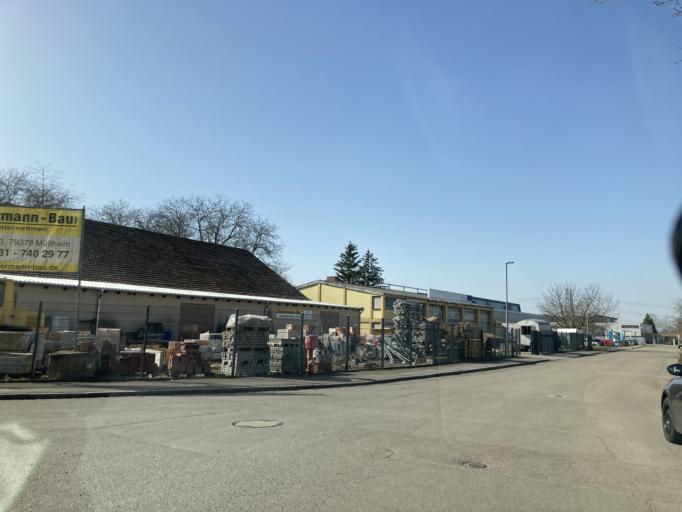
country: DE
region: Baden-Wuerttemberg
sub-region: Freiburg Region
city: Auggen
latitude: 47.8133
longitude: 7.6000
